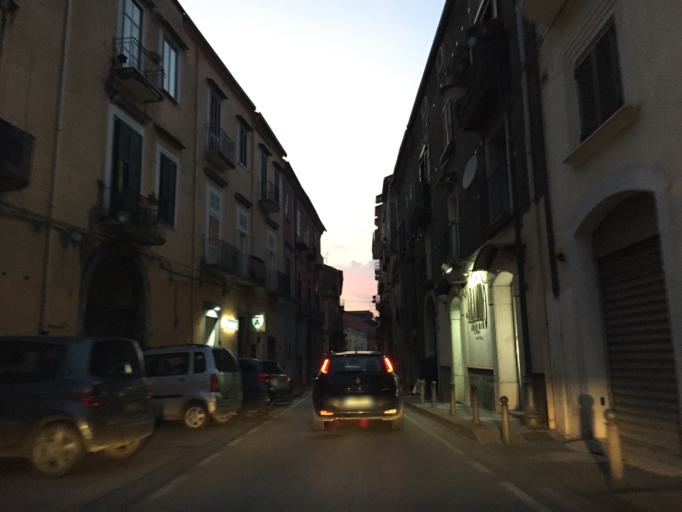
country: IT
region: Campania
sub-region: Provincia di Salerno
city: Nocera Inferiore
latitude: 40.7474
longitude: 14.6408
